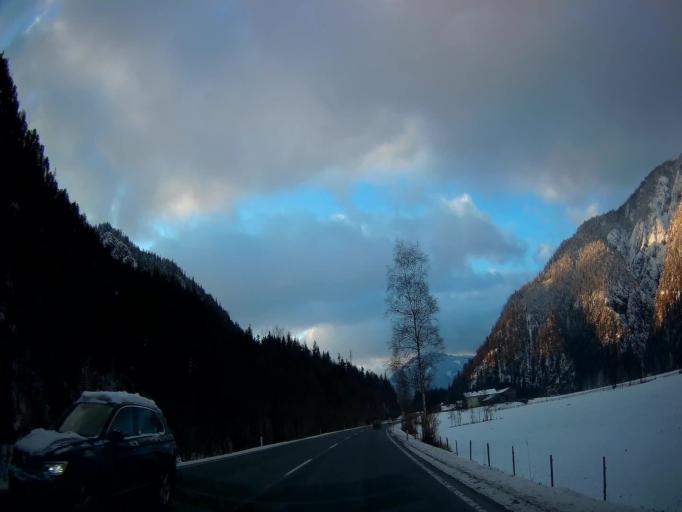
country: AT
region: Salzburg
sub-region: Politischer Bezirk Zell am See
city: Saalfelden am Steinernen Meer
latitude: 47.4724
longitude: 12.8313
